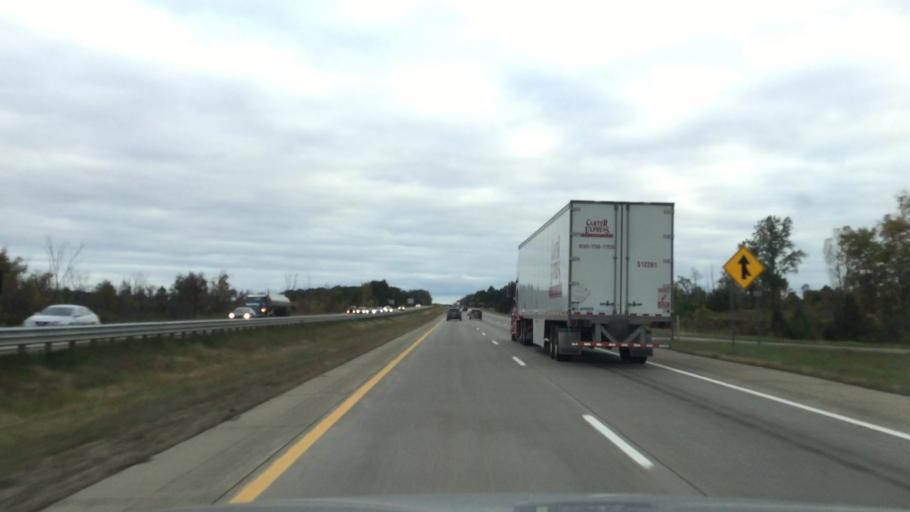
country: US
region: Michigan
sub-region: Genesee County
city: Lake Fenton
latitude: 42.8644
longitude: -83.7397
